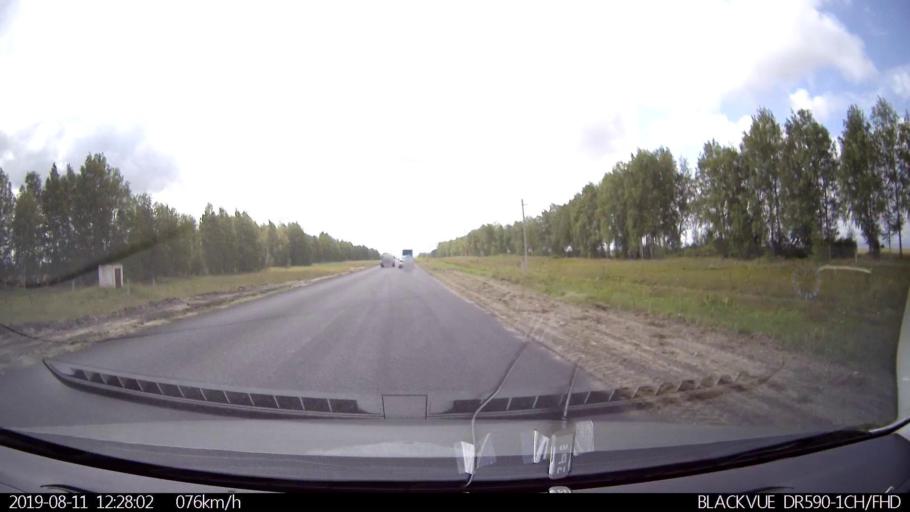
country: RU
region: Ulyanovsk
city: Ignatovka
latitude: 53.8479
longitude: 47.9151
